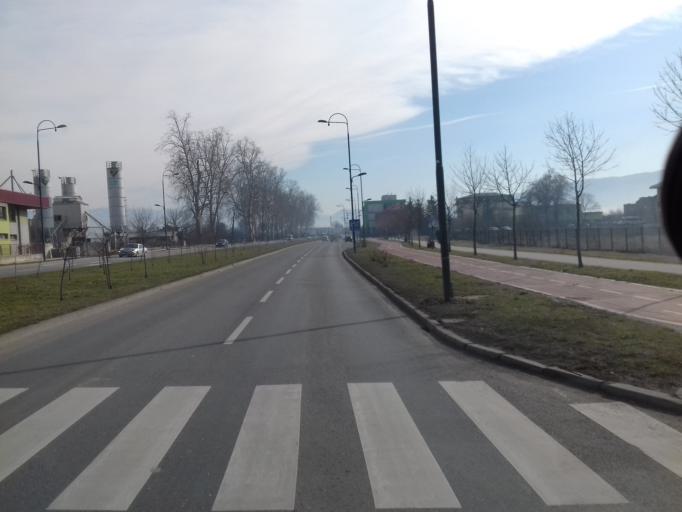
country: BA
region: Federation of Bosnia and Herzegovina
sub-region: Kanton Sarajevo
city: Sarajevo
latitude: 43.8282
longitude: 18.3147
